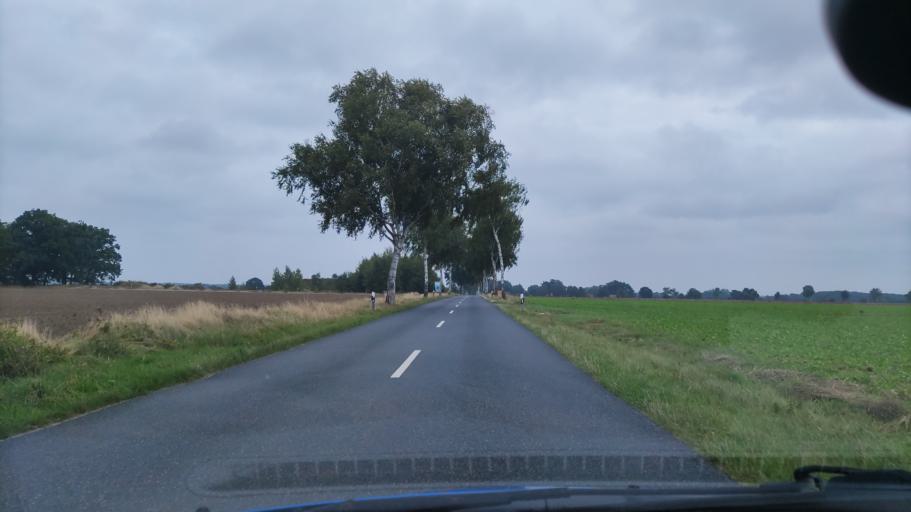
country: DE
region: Lower Saxony
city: Bienenbuttel
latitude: 53.1451
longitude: 10.5208
